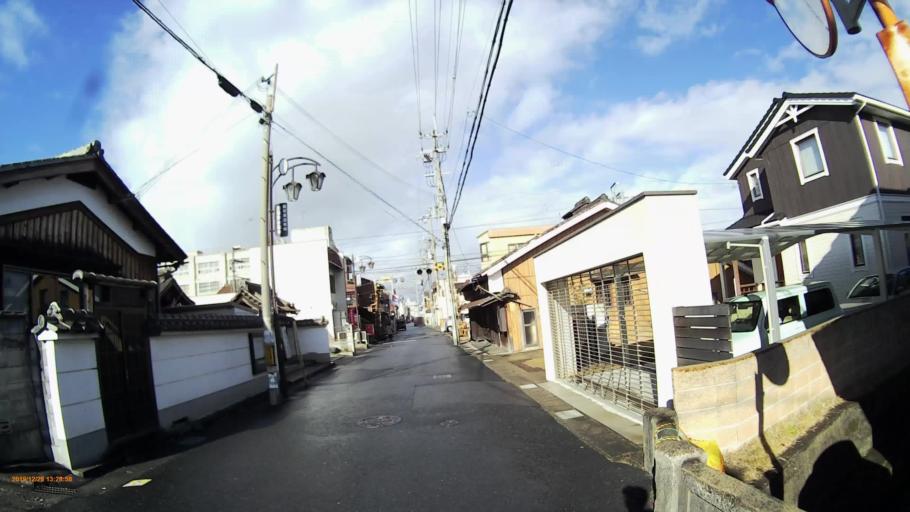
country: JP
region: Shiga Prefecture
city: Otsu-shi
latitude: 34.9882
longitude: 135.8942
